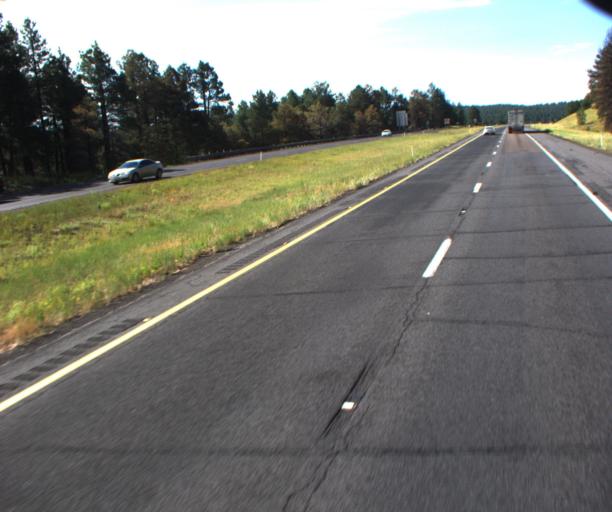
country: US
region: Arizona
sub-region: Coconino County
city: Kachina Village
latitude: 35.1098
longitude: -111.6816
